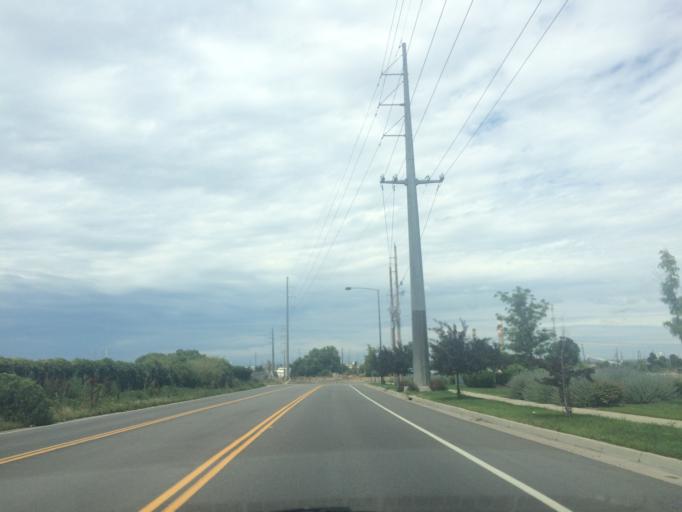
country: US
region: Colorado
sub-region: Adams County
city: Commerce City
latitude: 39.7962
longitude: -104.9585
